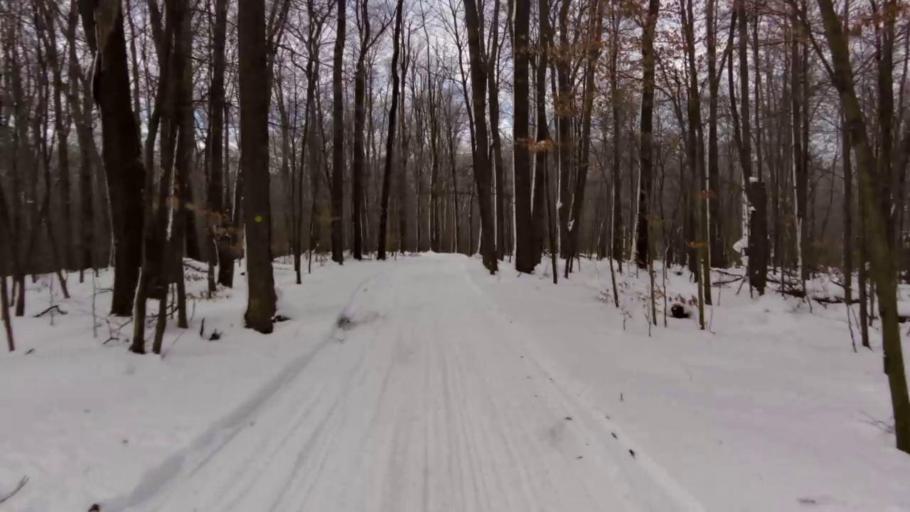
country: US
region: New York
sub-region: Cattaraugus County
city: Salamanca
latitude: 42.0354
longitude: -78.7523
